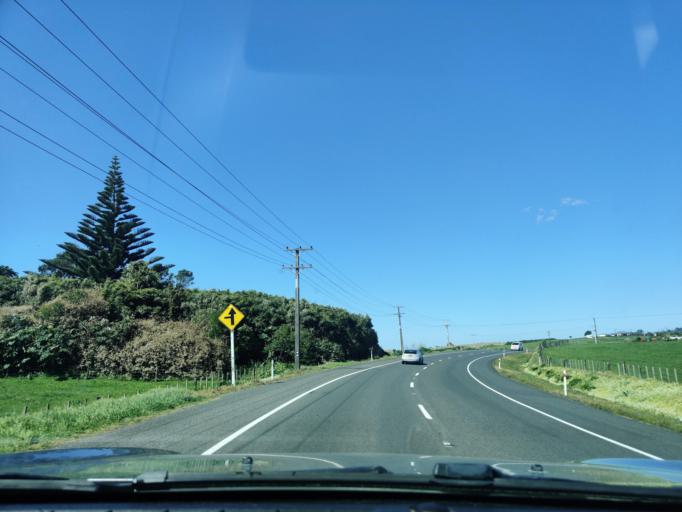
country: NZ
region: Taranaki
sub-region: New Plymouth District
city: New Plymouth
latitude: -39.0956
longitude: 173.9982
